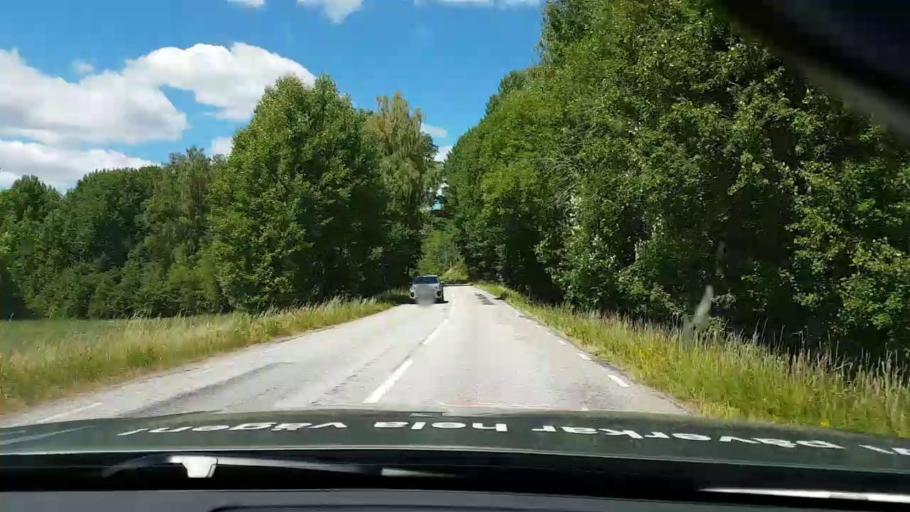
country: SE
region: Kalmar
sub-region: Vasterviks Kommun
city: Overum
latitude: 58.0640
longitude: 16.3999
